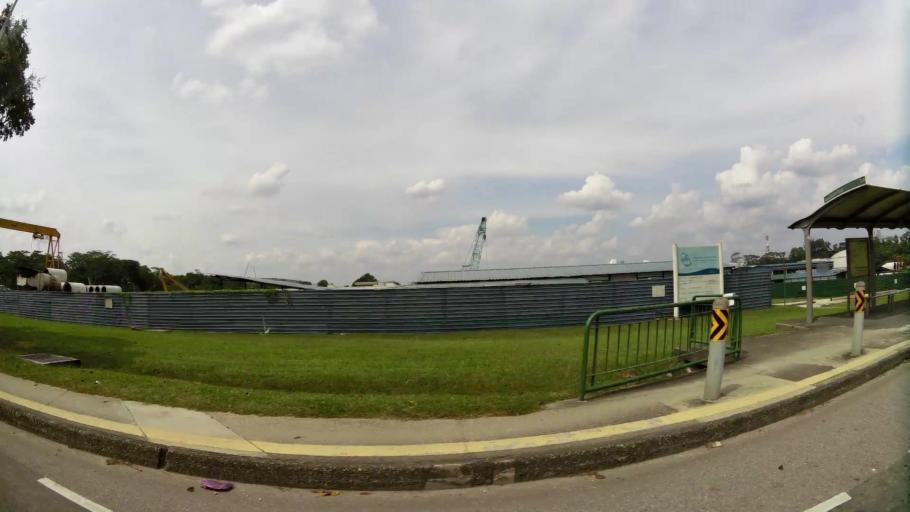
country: MY
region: Johor
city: Johor Bahru
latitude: 1.4241
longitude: 103.7586
